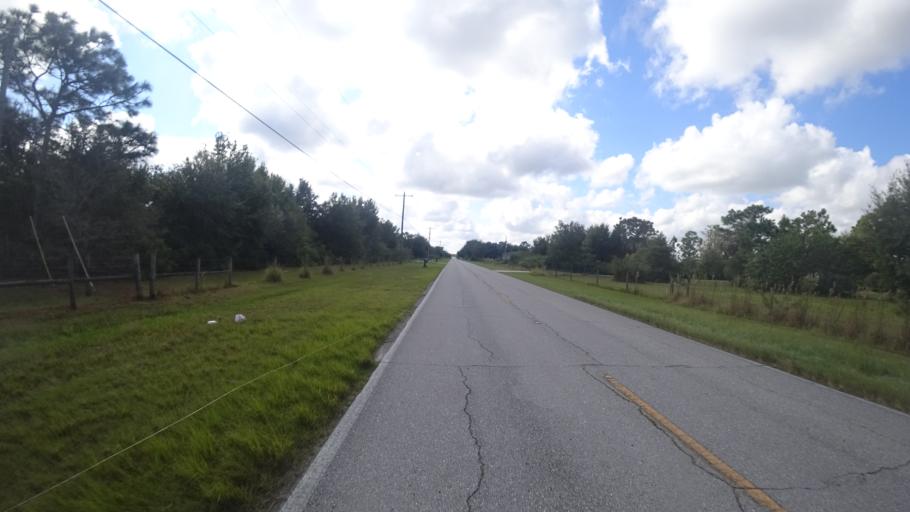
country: US
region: Florida
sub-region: Sarasota County
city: Lake Sarasota
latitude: 27.3985
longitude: -82.2711
